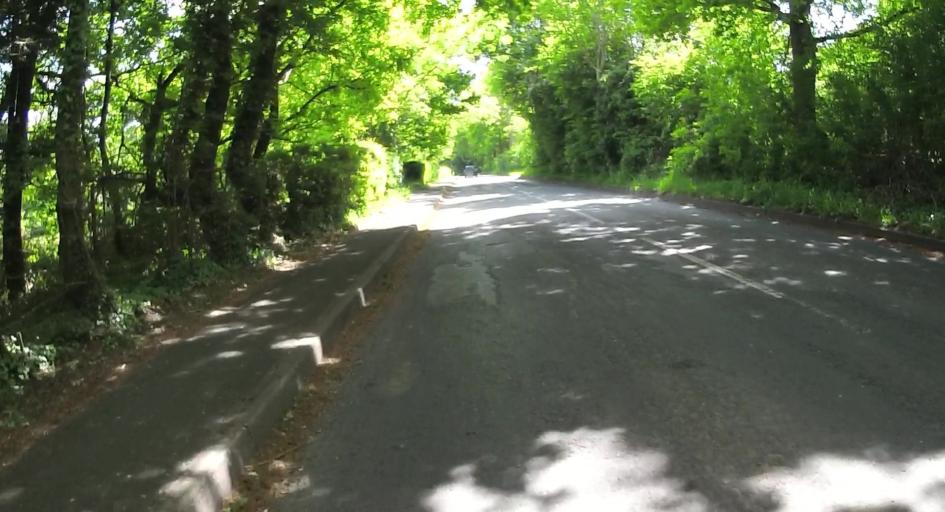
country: GB
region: England
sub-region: Hampshire
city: Fleet
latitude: 51.2436
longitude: -0.8601
